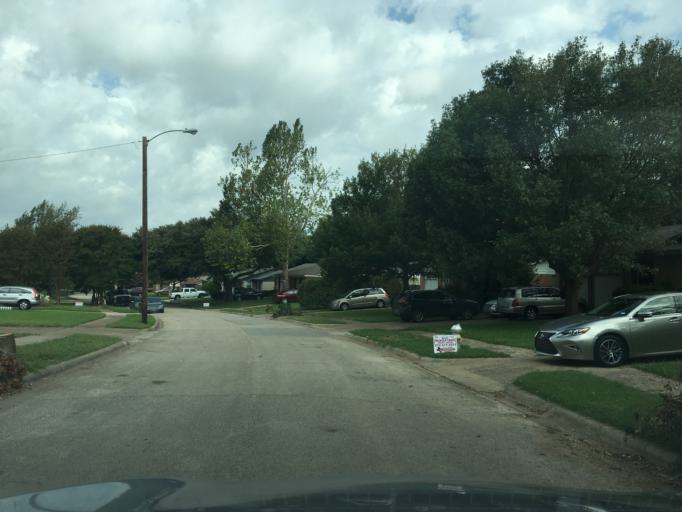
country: US
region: Texas
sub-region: Dallas County
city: Richardson
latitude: 32.8972
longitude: -96.7552
